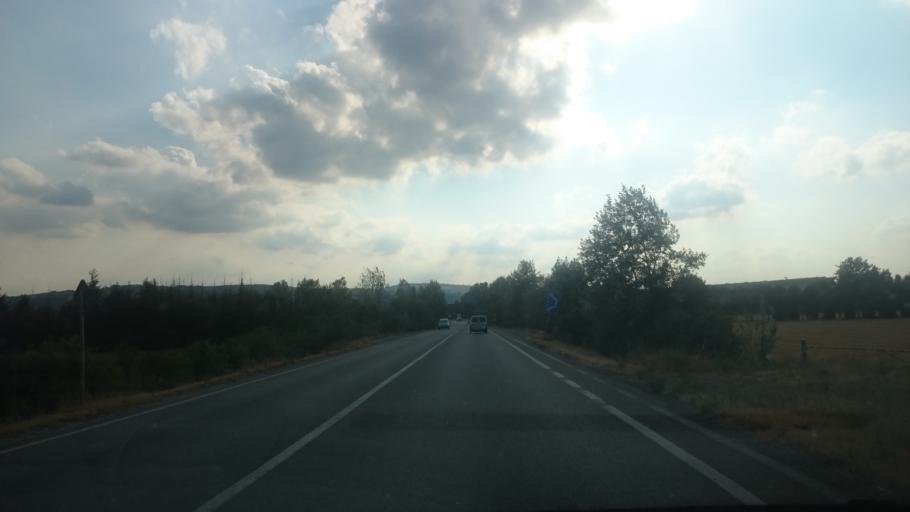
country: IT
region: Emilia-Romagna
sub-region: Provincia di Reggio Emilia
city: Salvaterra
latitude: 44.5902
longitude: 10.7697
